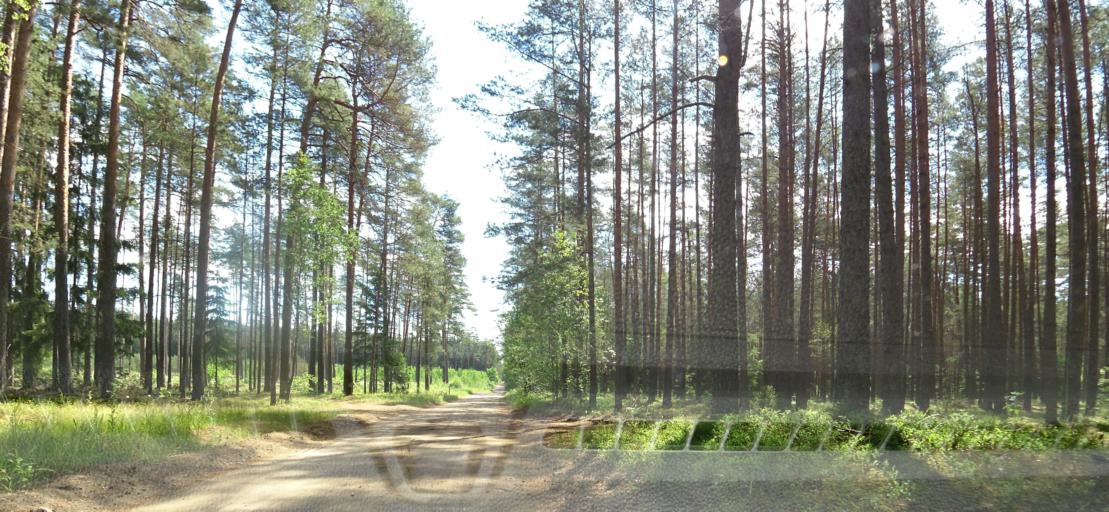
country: LT
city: Nemencine
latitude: 54.8317
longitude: 25.4361
